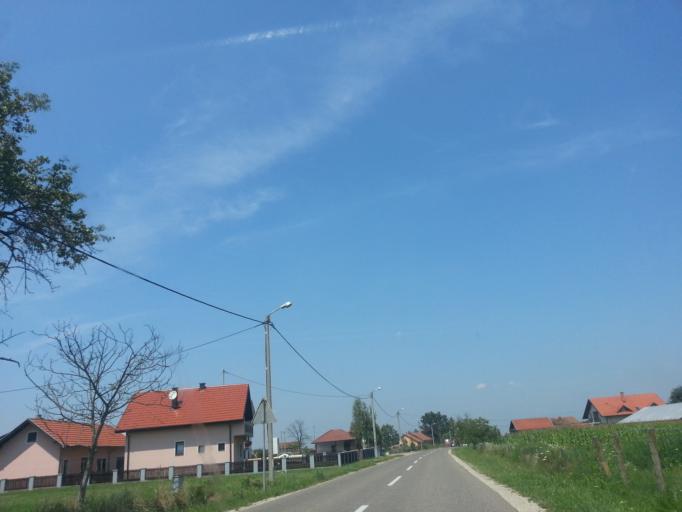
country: BA
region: Brcko
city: Brcko
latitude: 44.8027
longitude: 18.8413
